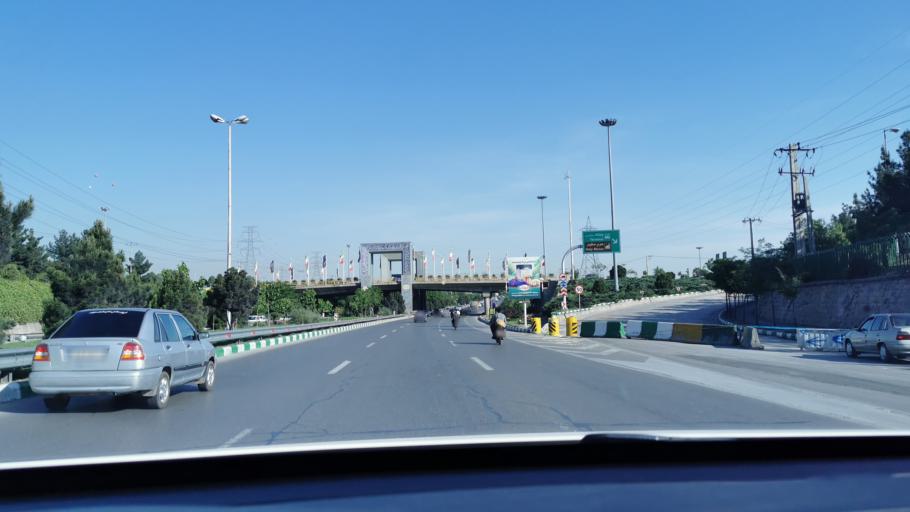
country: IR
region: Razavi Khorasan
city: Mashhad
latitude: 36.2618
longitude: 59.5844
